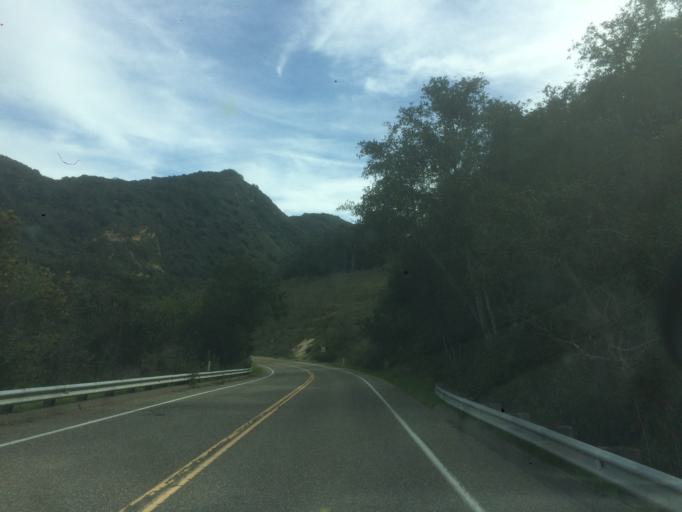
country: US
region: California
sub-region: San Luis Obispo County
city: Arroyo Grande
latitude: 35.1853
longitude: -120.4821
